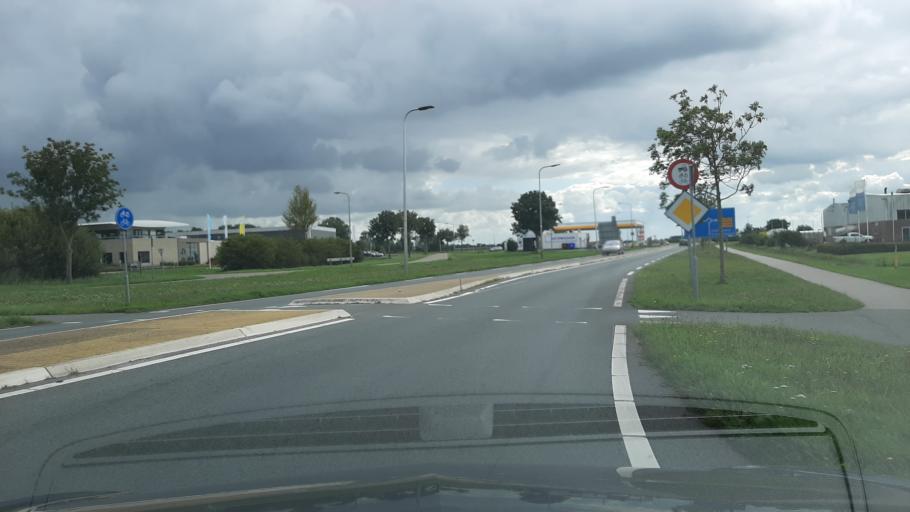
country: NL
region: Overijssel
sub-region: Gemeente Steenwijkerland
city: Tuk
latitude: 52.7790
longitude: 6.0987
